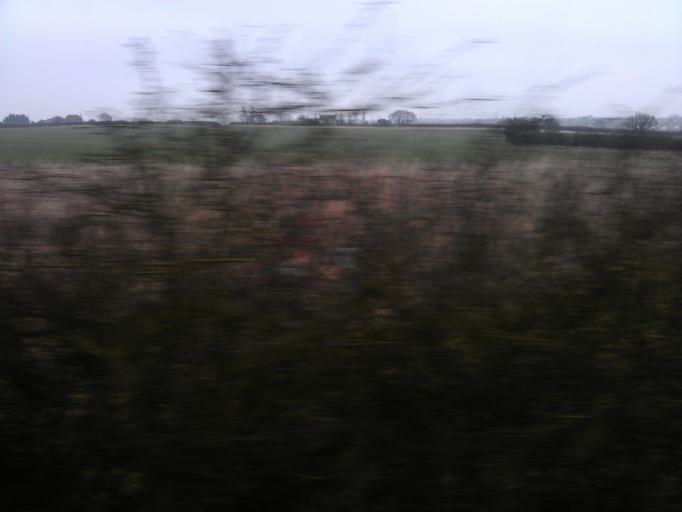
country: GB
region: England
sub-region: Essex
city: Clacton-on-Sea
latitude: 51.8168
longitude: 1.1798
